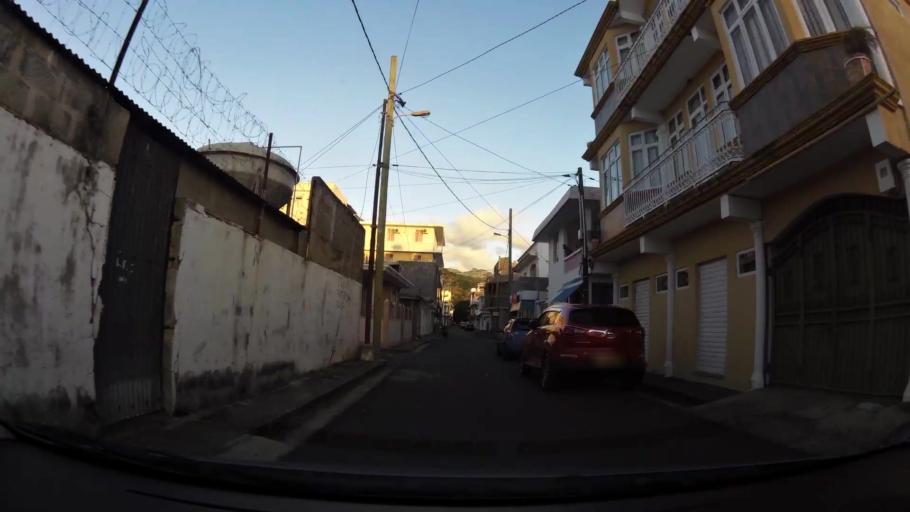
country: MU
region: Port Louis
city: Port Louis
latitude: -20.1542
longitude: 57.5124
